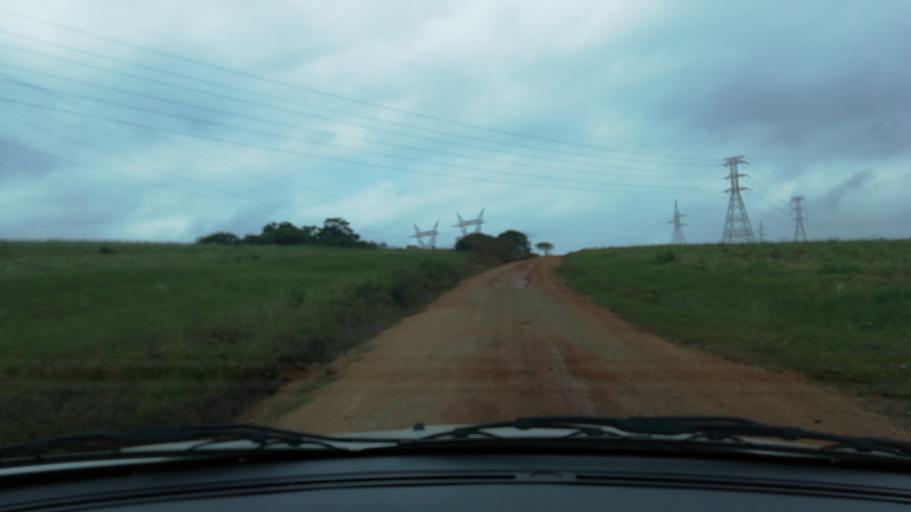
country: ZA
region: KwaZulu-Natal
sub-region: uThungulu District Municipality
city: Empangeni
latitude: -28.7325
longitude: 31.9001
